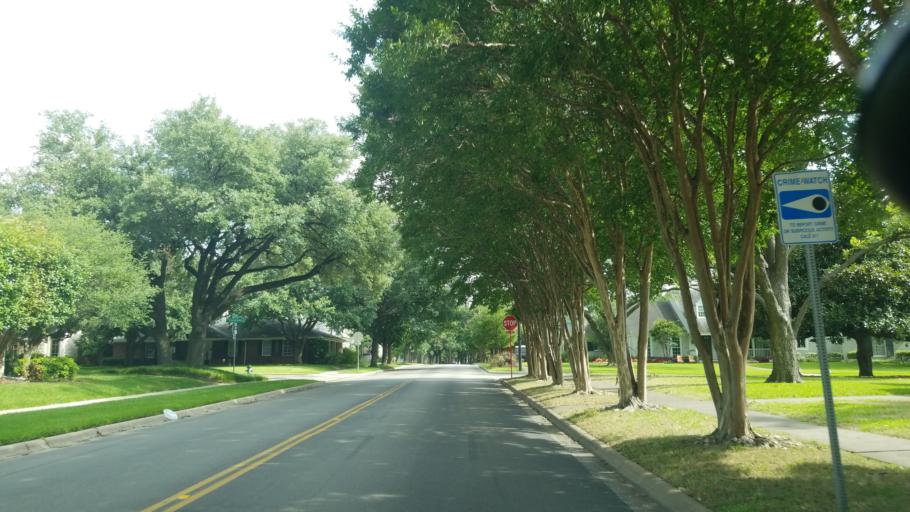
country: US
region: Texas
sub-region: Dallas County
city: University Park
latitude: 32.8648
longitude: -96.7921
